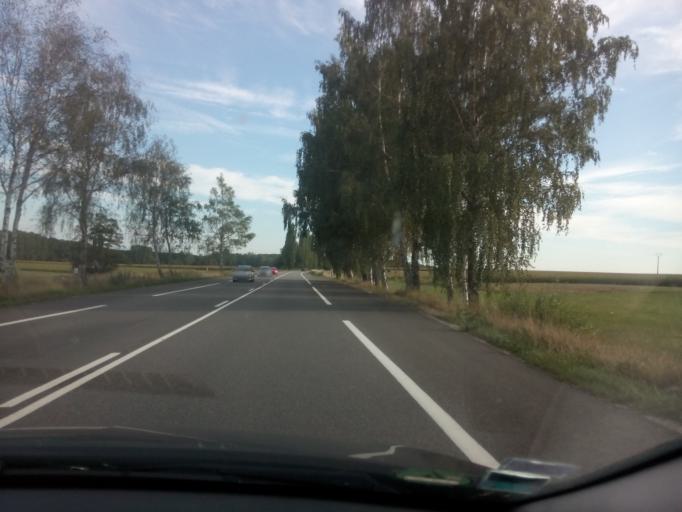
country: FR
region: Alsace
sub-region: Departement du Bas-Rhin
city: Soultz-sous-Forets
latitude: 48.9564
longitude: 7.9552
